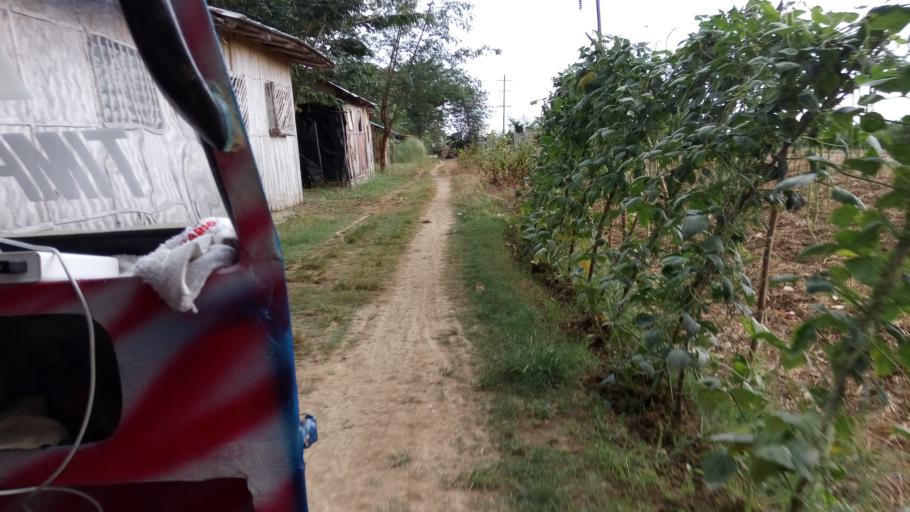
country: PH
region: Ilocos
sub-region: Province of La Union
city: Santo Tomas
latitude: 16.2750
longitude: 120.3887
